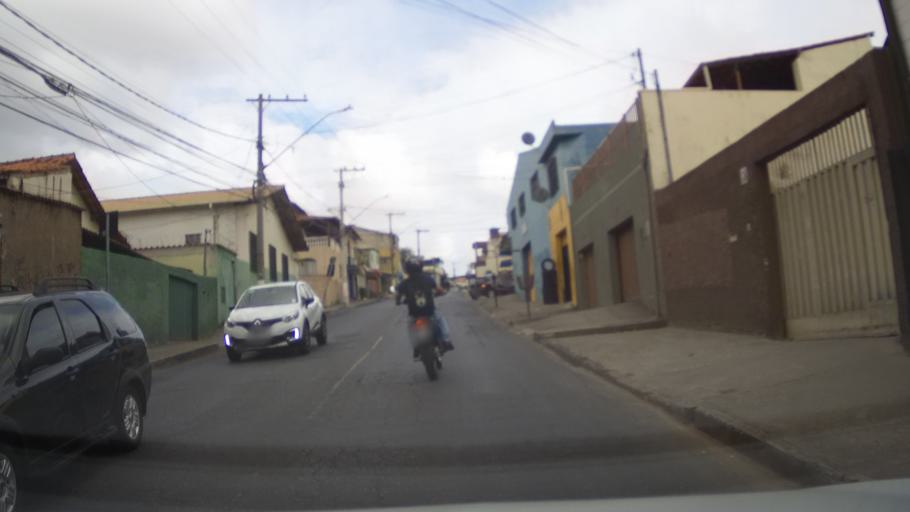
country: BR
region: Minas Gerais
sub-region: Belo Horizonte
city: Belo Horizonte
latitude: -19.8434
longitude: -43.9474
